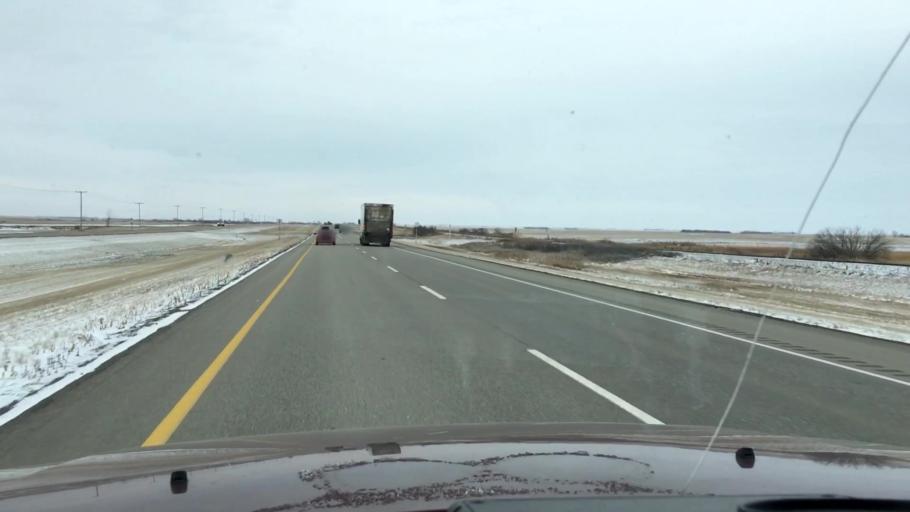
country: CA
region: Saskatchewan
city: Watrous
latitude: 51.1846
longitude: -105.9430
